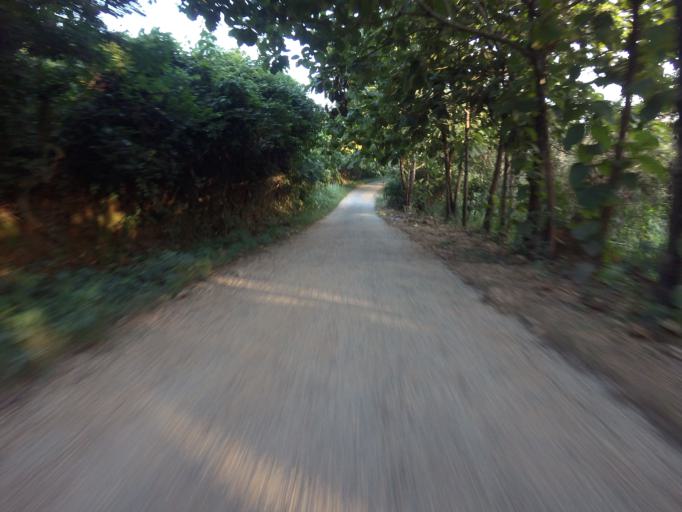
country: TG
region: Plateaux
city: Kpalime
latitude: 6.8881
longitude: 0.4473
